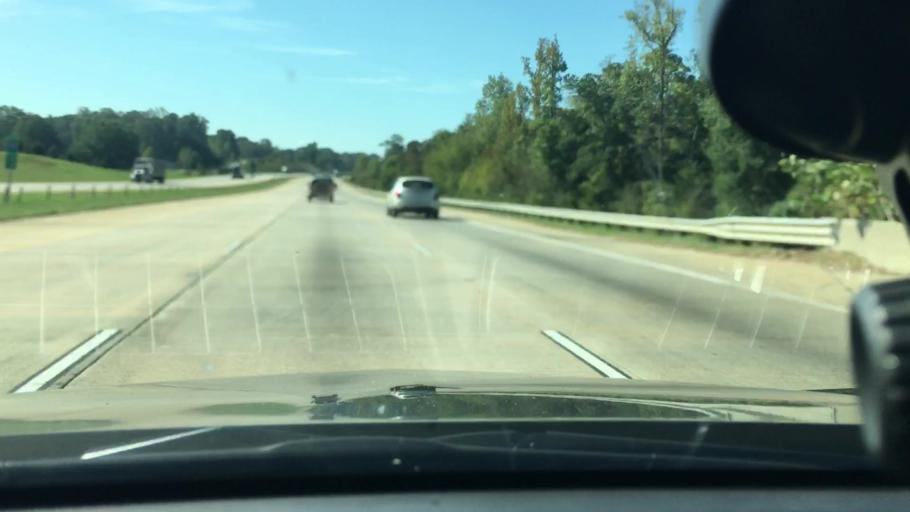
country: US
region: North Carolina
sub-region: Gaston County
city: Mount Holly
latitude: 35.3042
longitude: -80.9550
